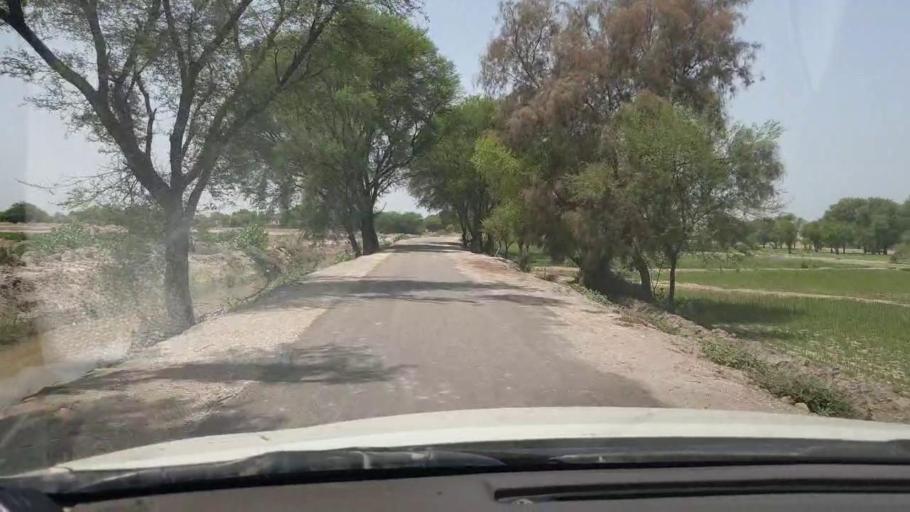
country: PK
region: Sindh
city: Rohri
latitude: 27.5160
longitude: 69.1815
